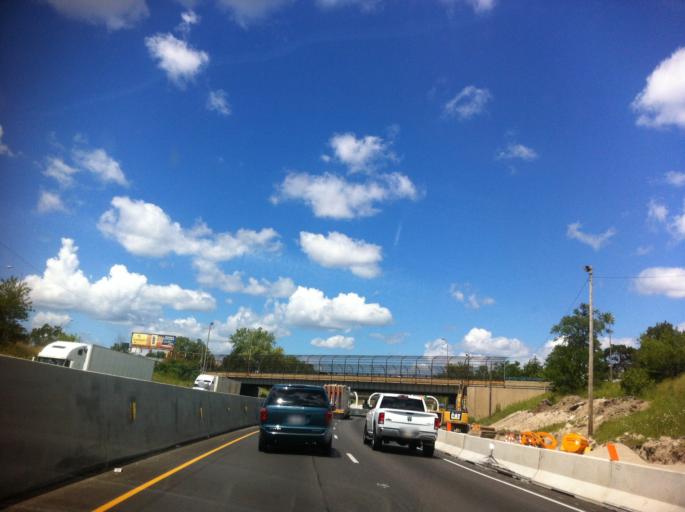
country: US
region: Ohio
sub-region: Lucas County
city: Toledo
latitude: 41.6604
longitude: -83.5638
